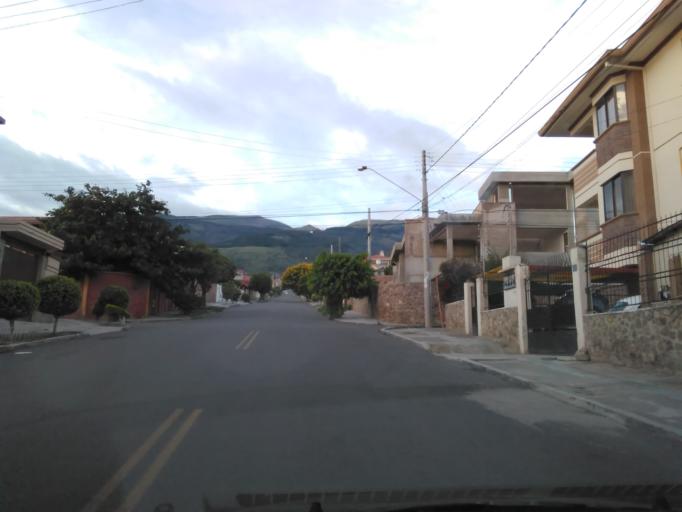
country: BO
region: Cochabamba
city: Cochabamba
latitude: -17.3620
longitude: -66.1564
